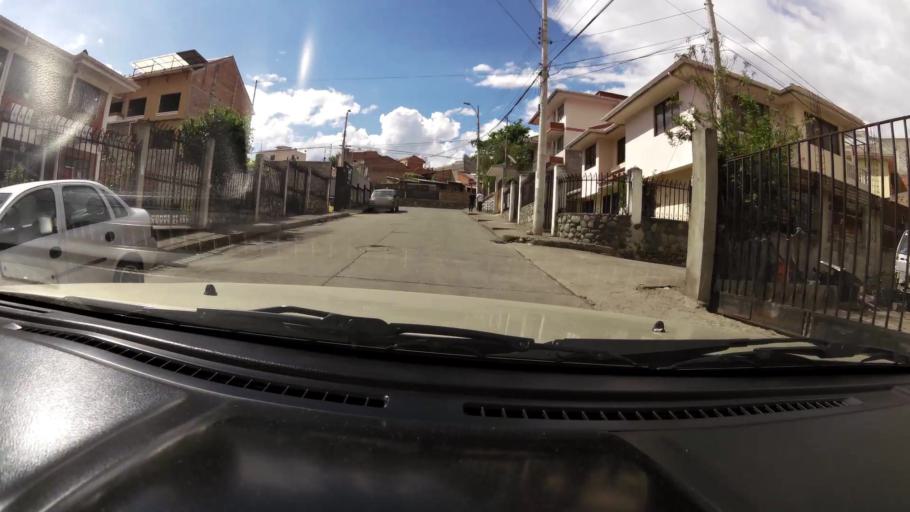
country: EC
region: Azuay
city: Cuenca
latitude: -2.8839
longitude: -78.9880
